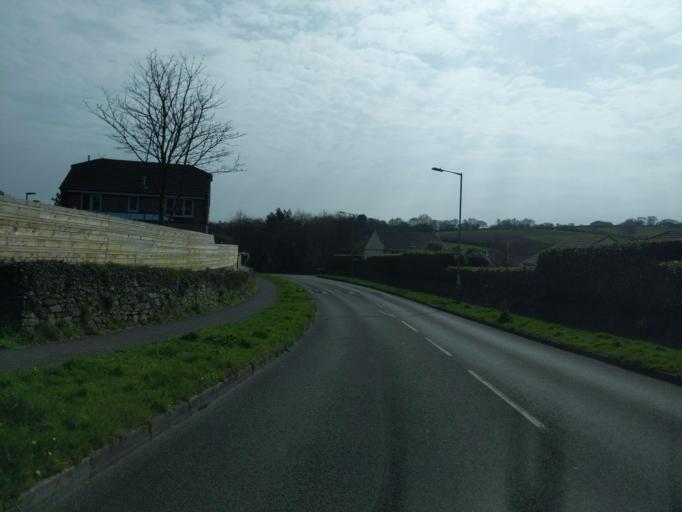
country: GB
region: England
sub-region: Cornwall
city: Saltash
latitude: 50.4096
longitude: -4.2410
